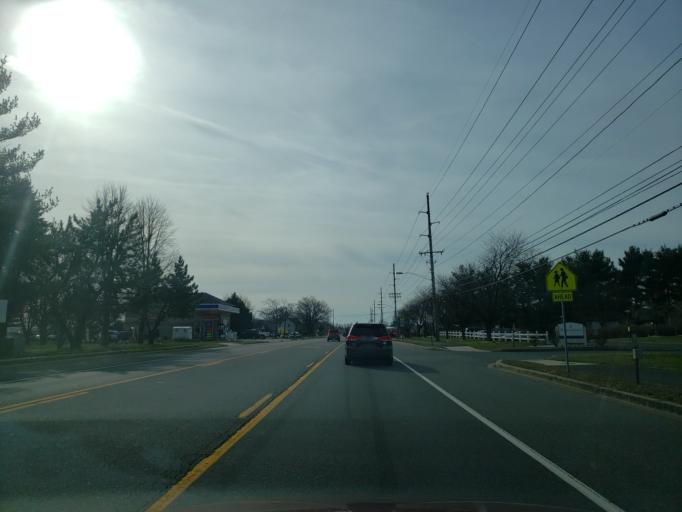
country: US
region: Delaware
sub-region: Kent County
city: Dover
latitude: 39.1633
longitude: -75.5444
